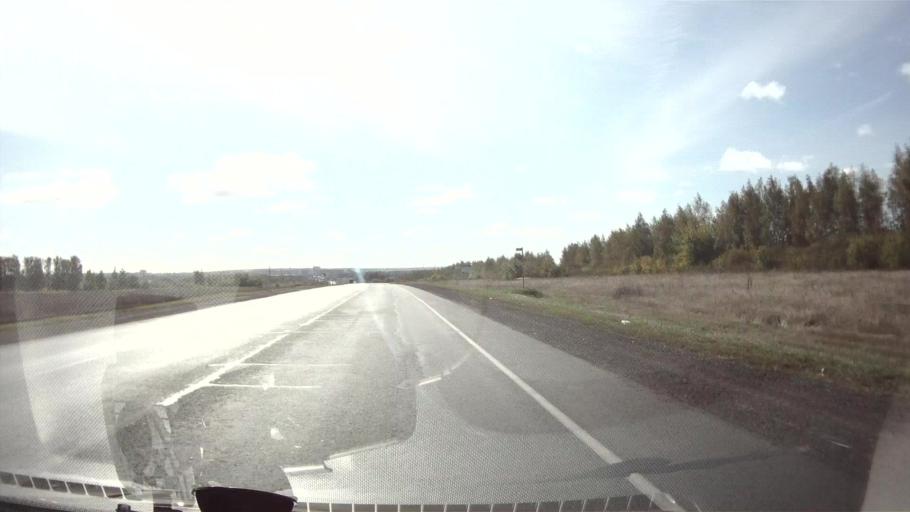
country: RU
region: Ulyanovsk
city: Isheyevka
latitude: 54.3138
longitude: 48.2342
